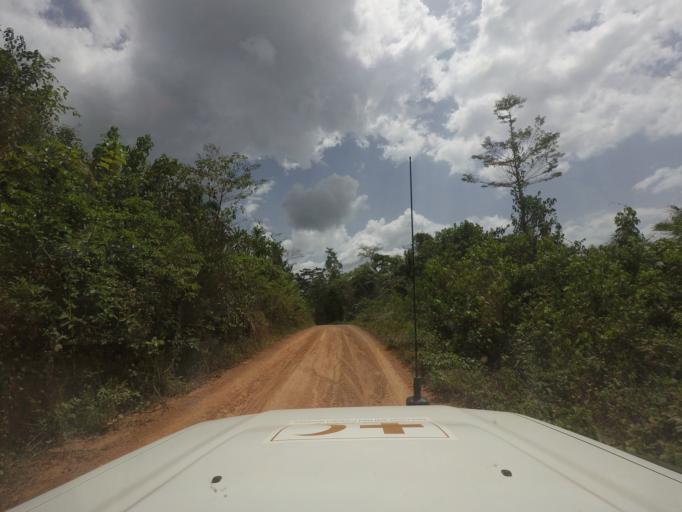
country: LR
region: Bong
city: Gbarnga
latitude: 7.0581
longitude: -9.2384
